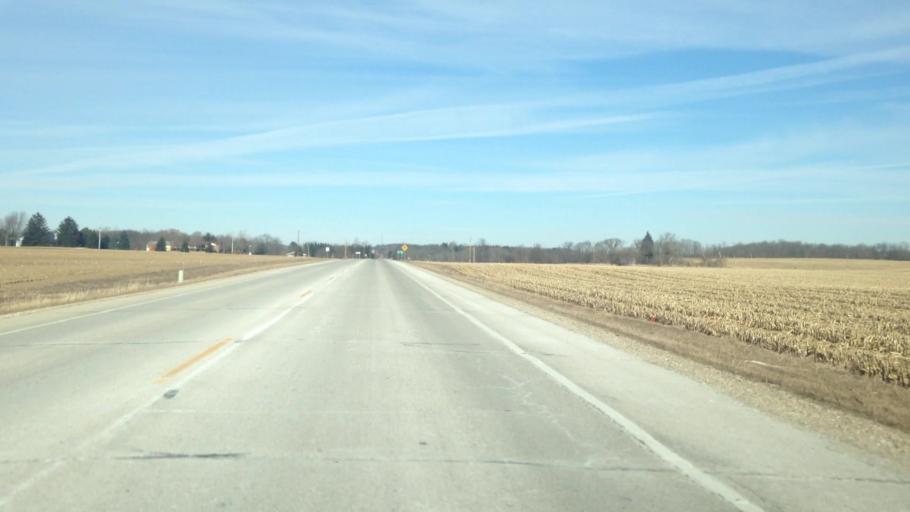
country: US
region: Wisconsin
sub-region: Washington County
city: Slinger
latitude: 43.2770
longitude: -88.2613
